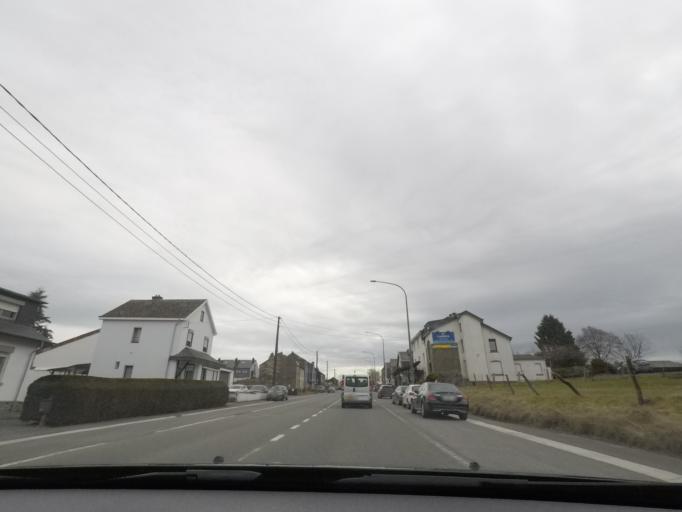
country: BE
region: Wallonia
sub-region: Province du Luxembourg
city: Bastogne
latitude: 49.9961
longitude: 5.7220
